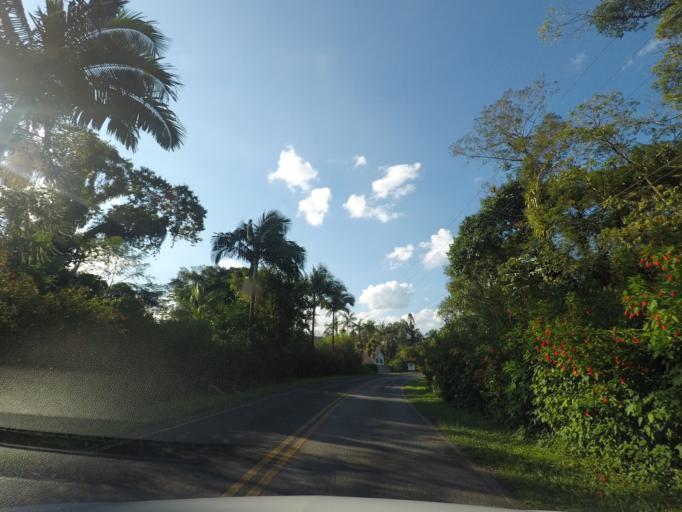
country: BR
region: Parana
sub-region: Antonina
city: Antonina
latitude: -25.3998
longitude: -48.8722
